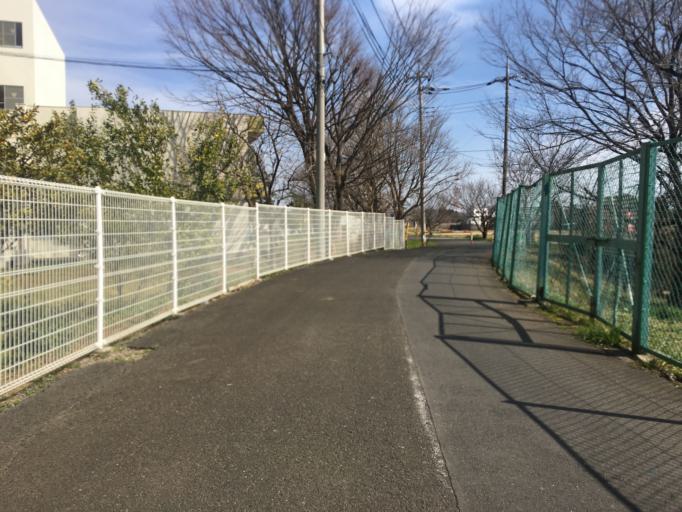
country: JP
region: Saitama
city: Shiki
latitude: 35.8310
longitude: 139.5923
